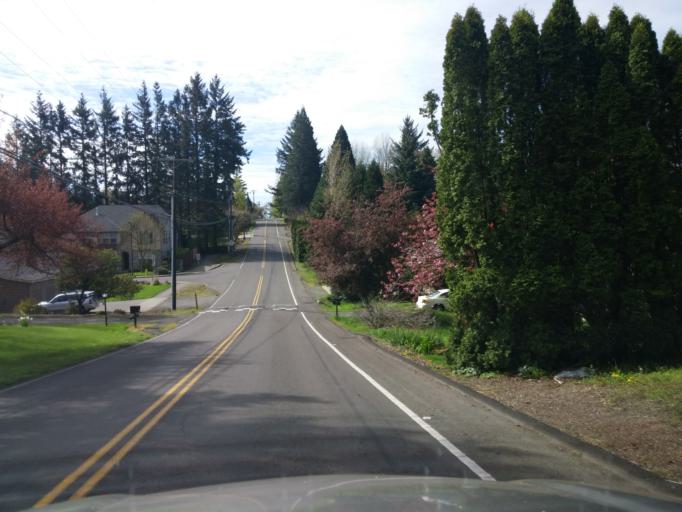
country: US
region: Oregon
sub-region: Washington County
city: Cedar Mill
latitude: 45.5382
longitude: -122.7907
